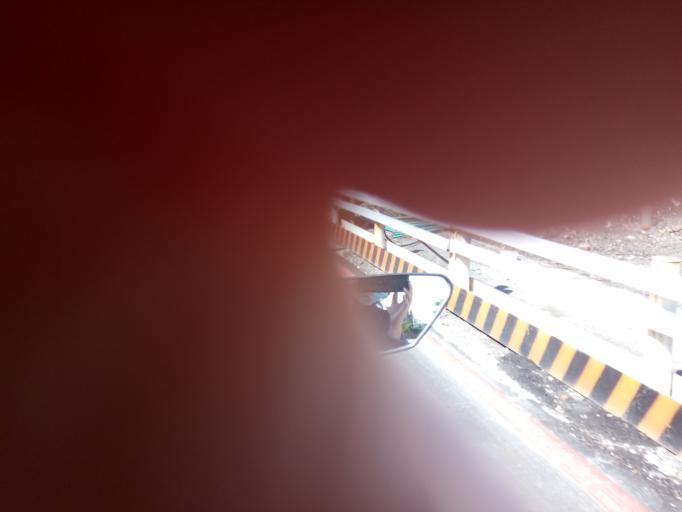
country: TW
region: Taiwan
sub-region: Yilan
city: Yilan
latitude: 24.6741
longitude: 121.7795
